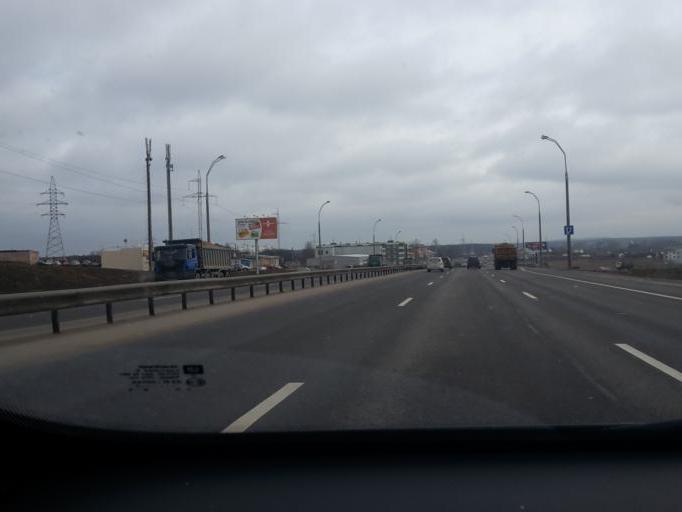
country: BY
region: Minsk
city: Zhdanovichy
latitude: 53.9350
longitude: 27.4257
